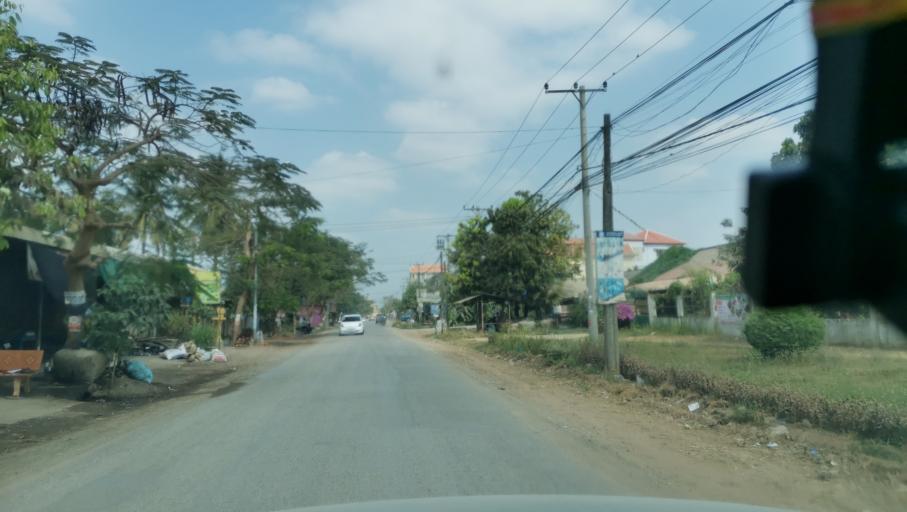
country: KH
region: Battambang
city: Battambang
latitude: 13.1117
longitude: 103.1963
